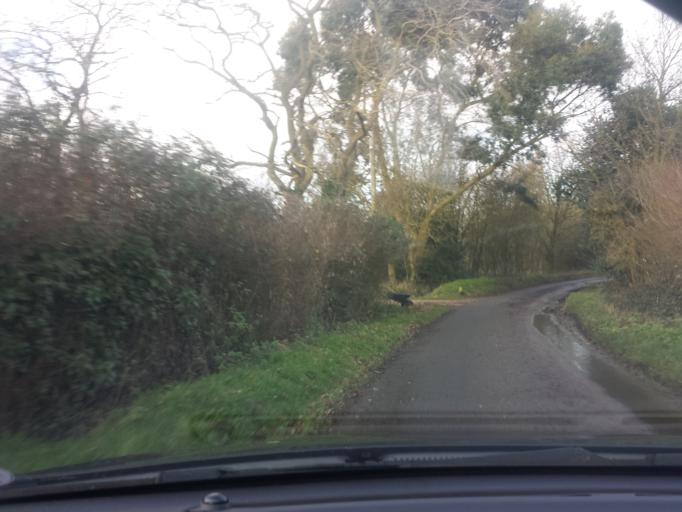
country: GB
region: England
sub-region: Essex
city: Manningtree
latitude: 51.9011
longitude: 1.0449
